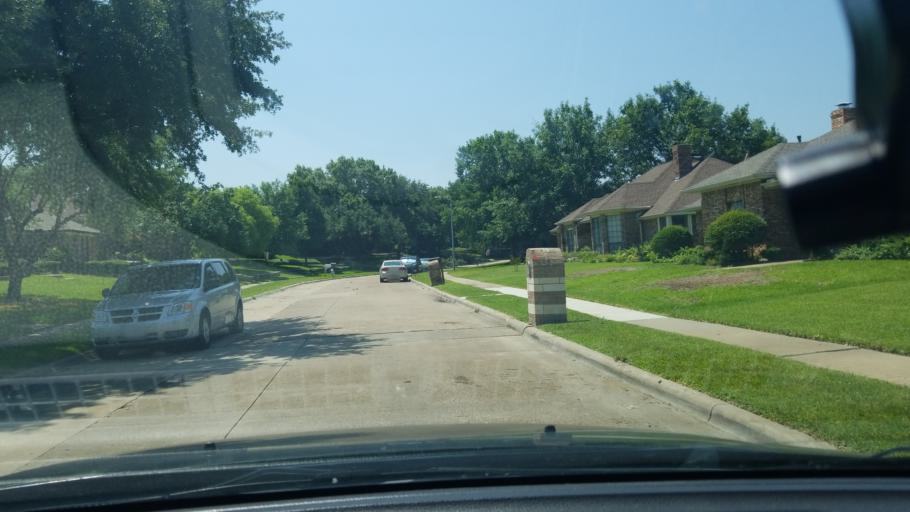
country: US
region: Texas
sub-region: Dallas County
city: Mesquite
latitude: 32.8284
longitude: -96.6162
